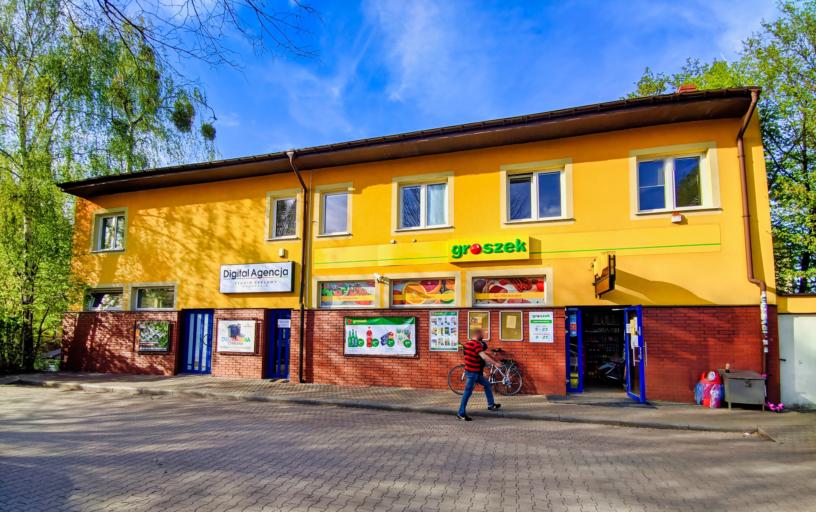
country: PL
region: Lubusz
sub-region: Powiat swiebodzinski
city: Swiebodzin
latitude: 52.2470
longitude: 15.5236
